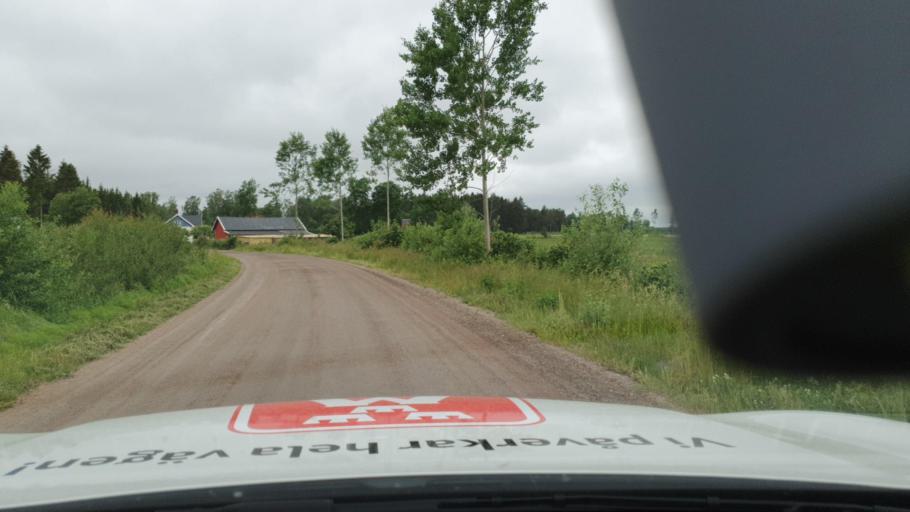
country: SE
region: Vaestra Goetaland
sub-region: Tidaholms Kommun
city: Olofstorp
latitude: 58.3547
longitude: 14.0453
